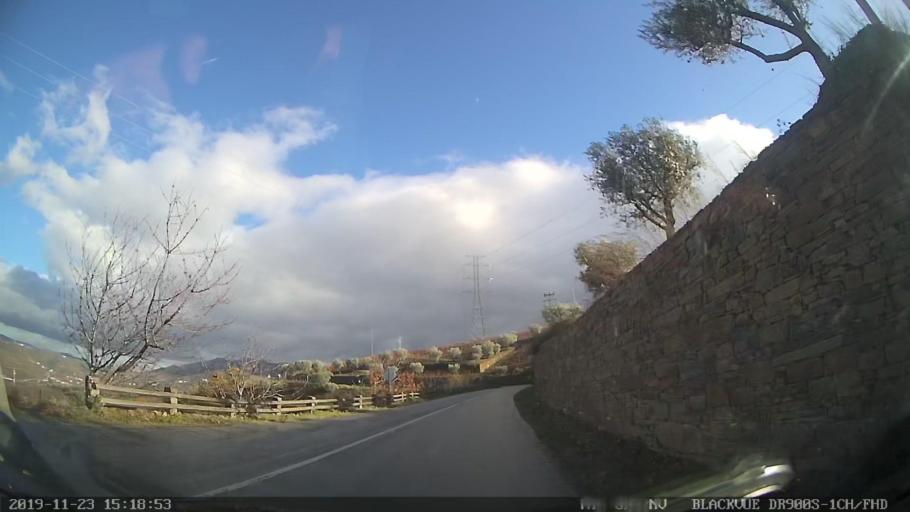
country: PT
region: Viseu
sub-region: Lamego
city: Lamego
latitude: 41.1181
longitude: -7.7929
